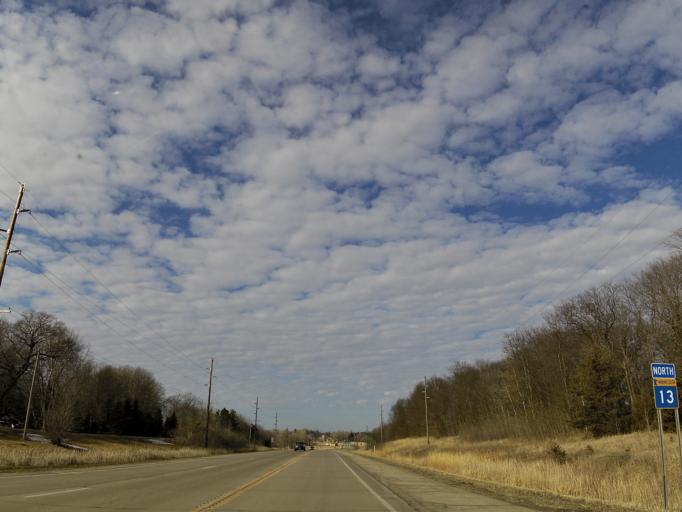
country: US
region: Minnesota
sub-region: Le Sueur County
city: New Prague
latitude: 44.5299
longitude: -93.5855
